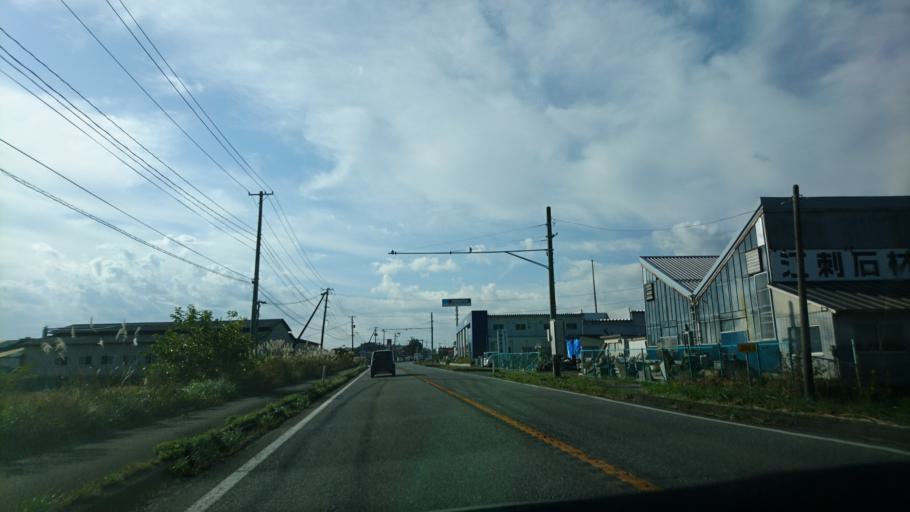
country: JP
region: Miyagi
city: Furukawa
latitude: 38.6102
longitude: 140.9830
